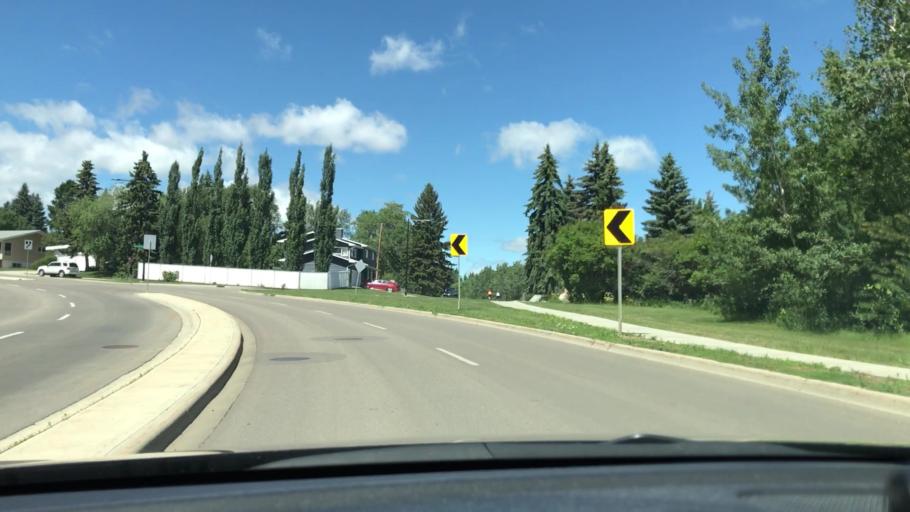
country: CA
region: Alberta
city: Edmonton
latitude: 53.5160
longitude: -113.5559
